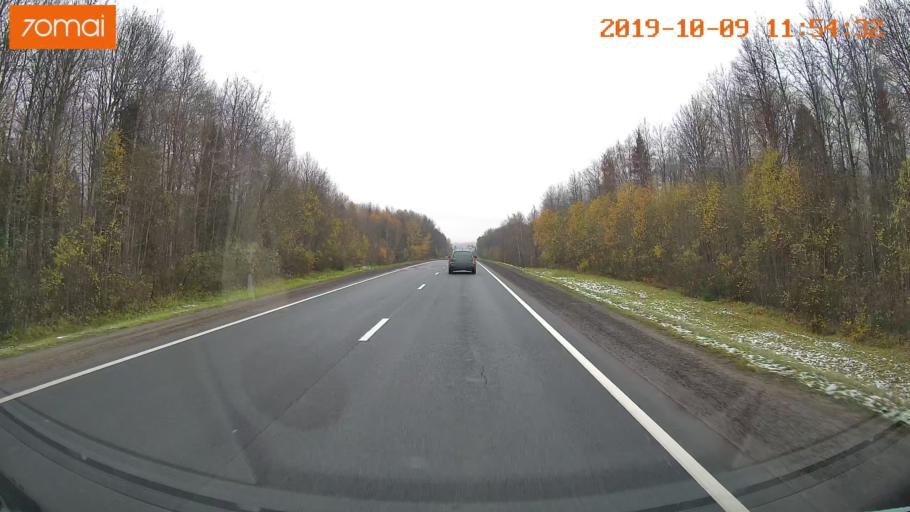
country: RU
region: Vologda
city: Gryazovets
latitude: 58.7581
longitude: 40.2818
